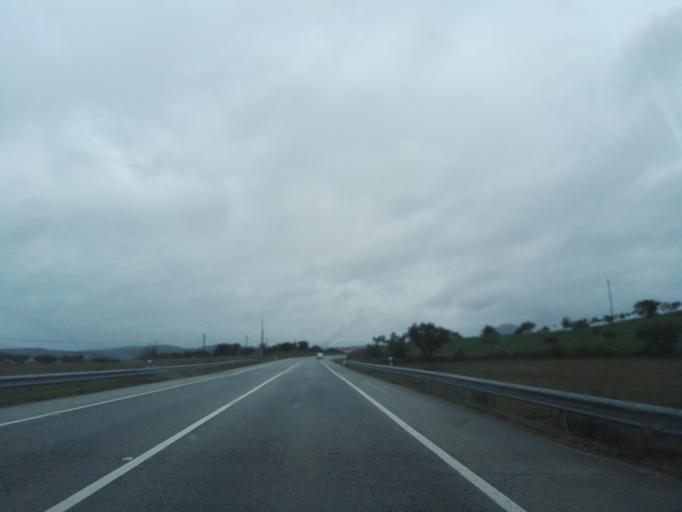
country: PT
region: Portalegre
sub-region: Portalegre
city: Urra
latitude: 39.2612
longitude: -7.4128
